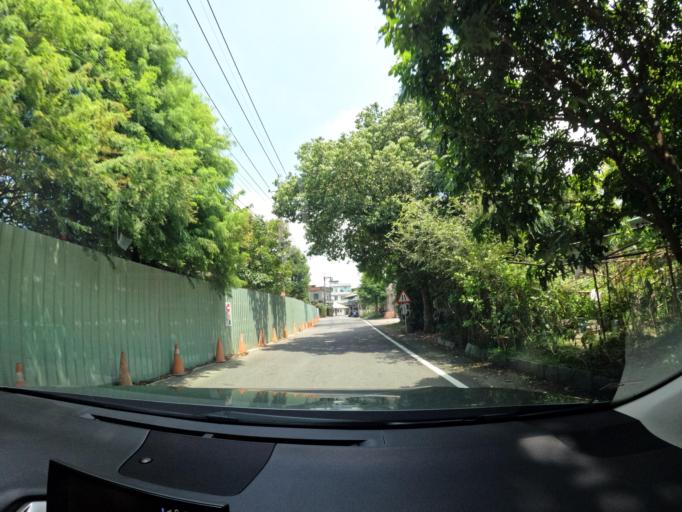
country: TW
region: Taiwan
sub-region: Miaoli
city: Miaoli
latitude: 24.4090
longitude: 120.7833
